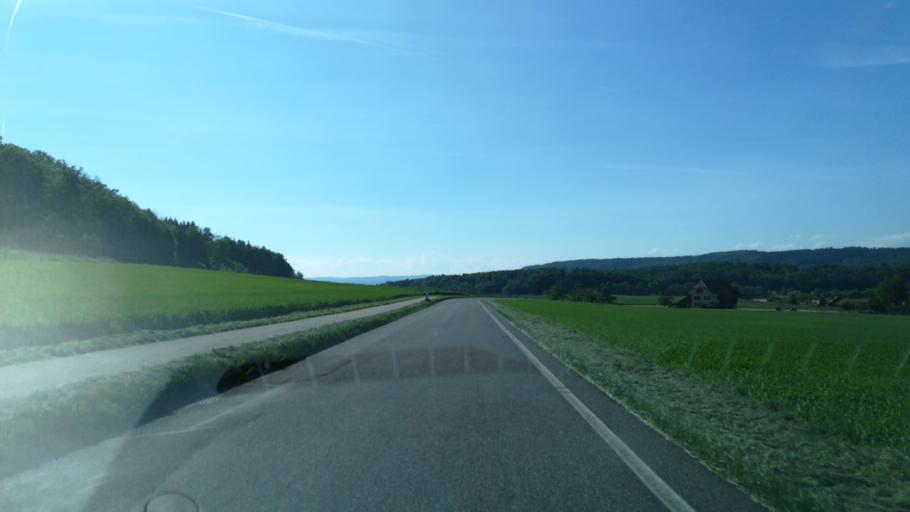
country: CH
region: Thurgau
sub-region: Frauenfeld District
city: Wagenhausen
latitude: 47.6686
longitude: 8.8119
